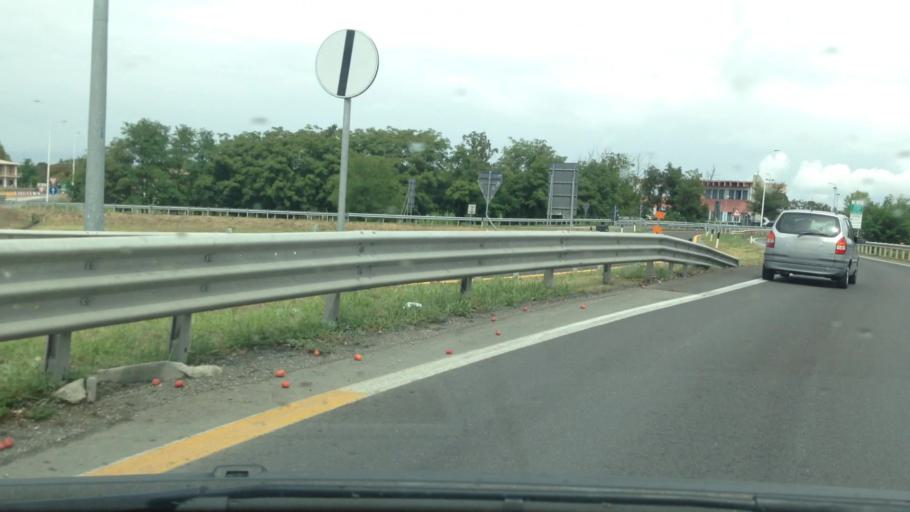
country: IT
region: Piedmont
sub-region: Provincia di Alessandria
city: Tortona
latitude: 44.9081
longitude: 8.8370
